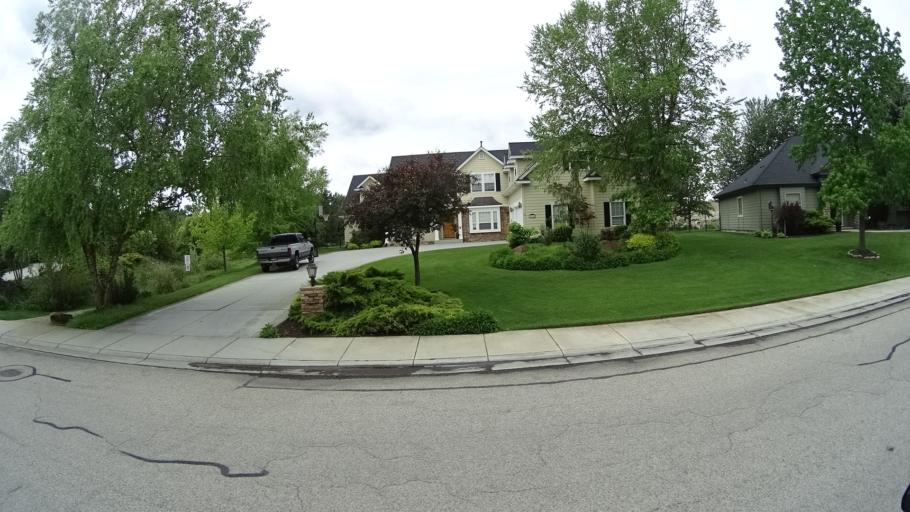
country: US
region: Idaho
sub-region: Ada County
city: Eagle
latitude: 43.6770
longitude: -116.3133
